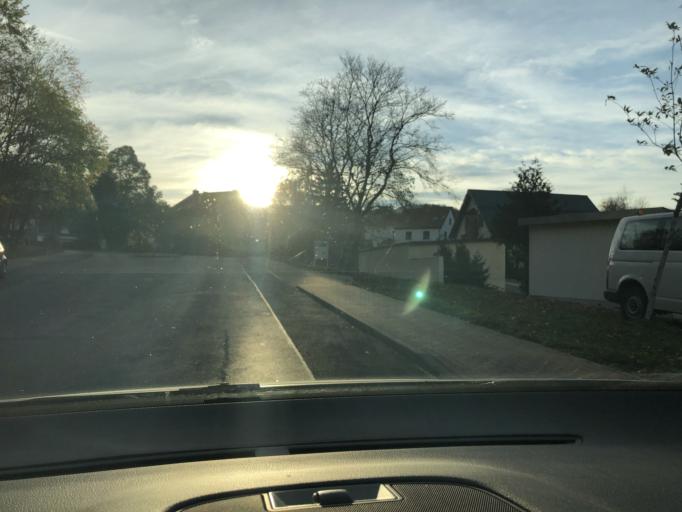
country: DE
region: Thuringia
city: Ilmenau
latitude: 50.6798
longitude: 10.9210
